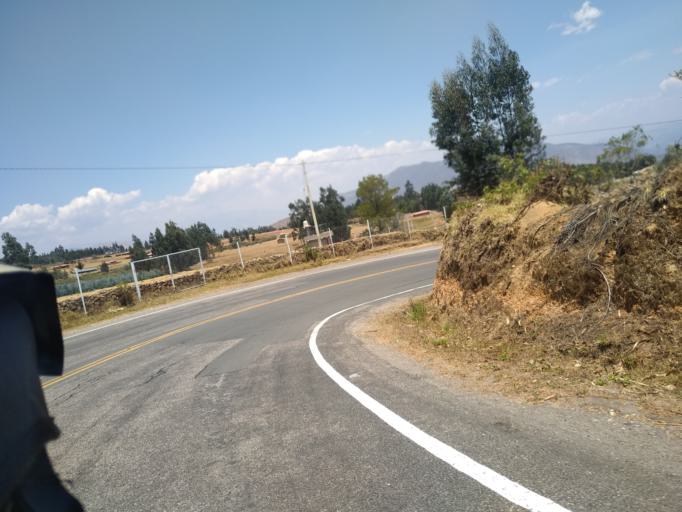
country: PE
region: Cajamarca
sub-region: San Marcos
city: San Marcos
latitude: -7.2875
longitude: -78.2055
